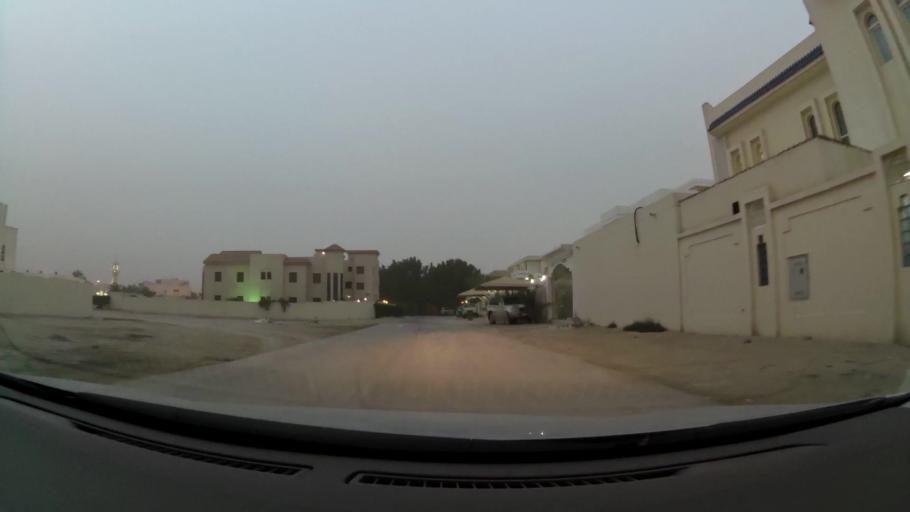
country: QA
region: Baladiyat ad Dawhah
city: Doha
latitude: 25.2296
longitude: 51.4927
